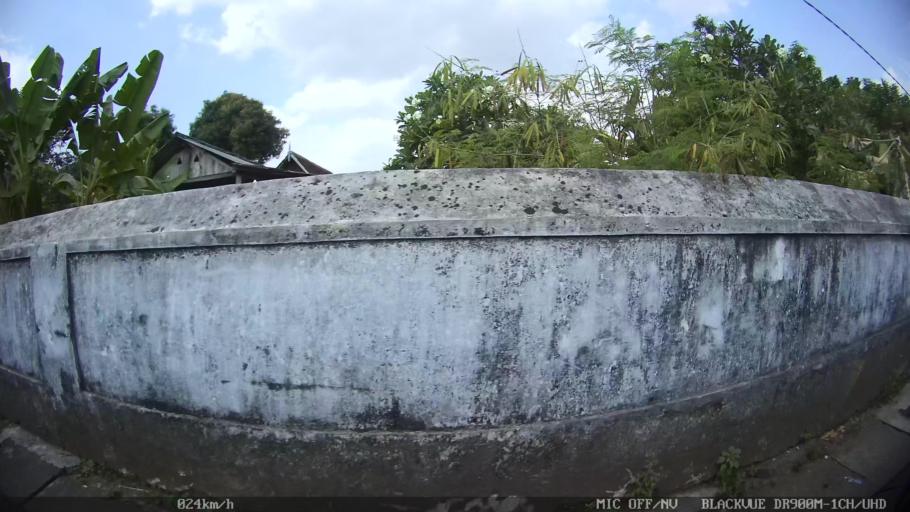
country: ID
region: Daerah Istimewa Yogyakarta
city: Yogyakarta
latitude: -7.8239
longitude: 110.3963
